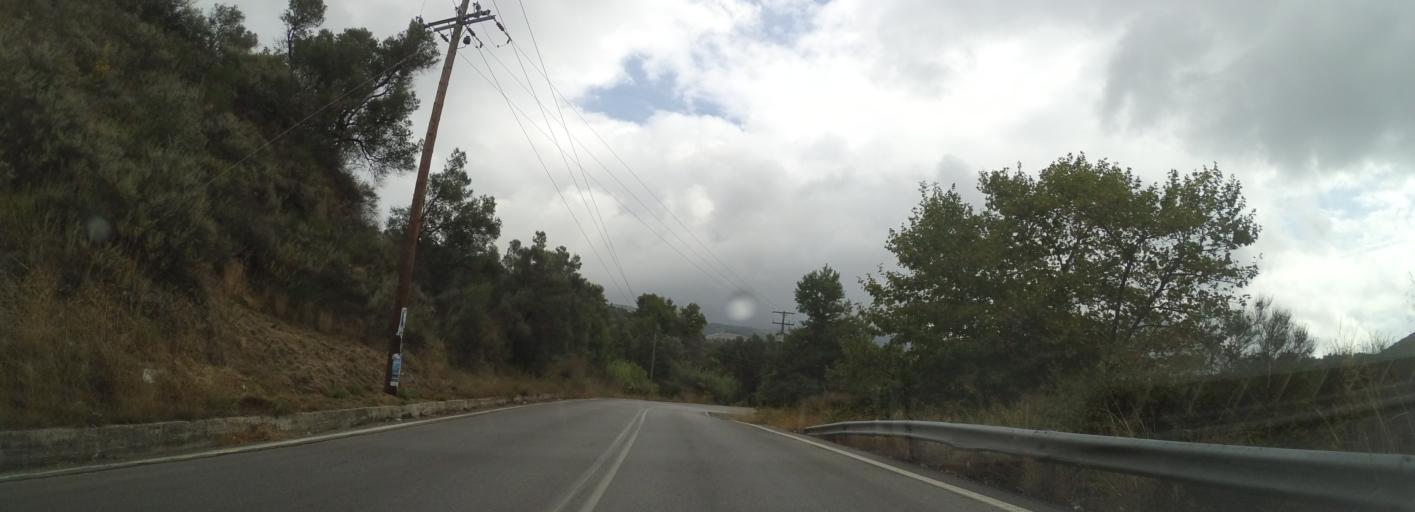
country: GR
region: Crete
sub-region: Nomos Rethymnis
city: Agia Foteini
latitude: 35.2205
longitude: 24.5127
